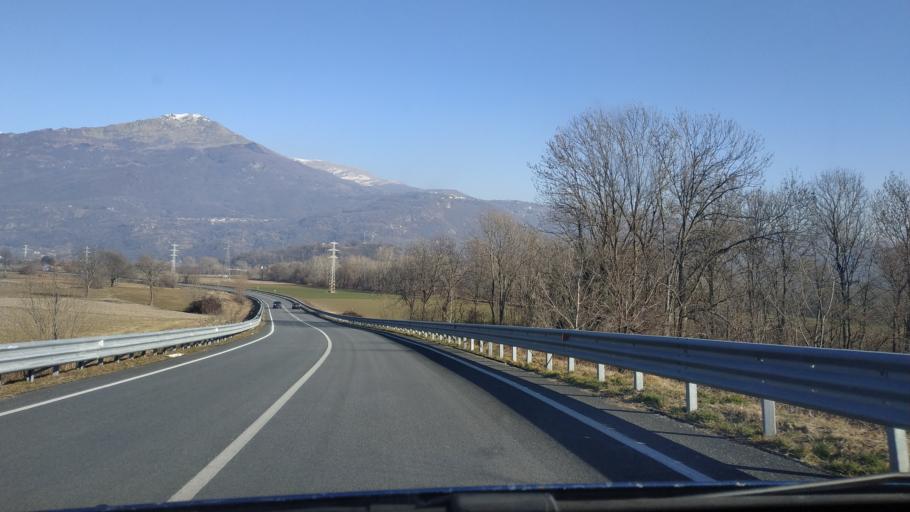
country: IT
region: Piedmont
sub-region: Provincia di Torino
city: Quassolo
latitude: 45.5014
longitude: 7.8332
